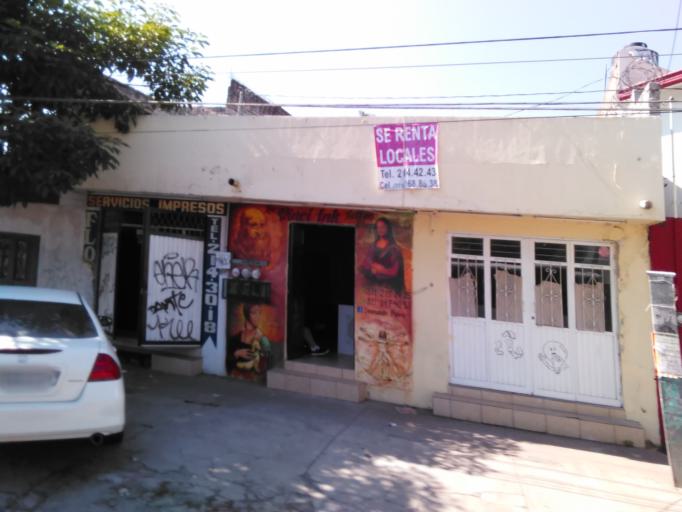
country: MX
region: Nayarit
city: Tepic
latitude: 21.4827
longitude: -104.8762
